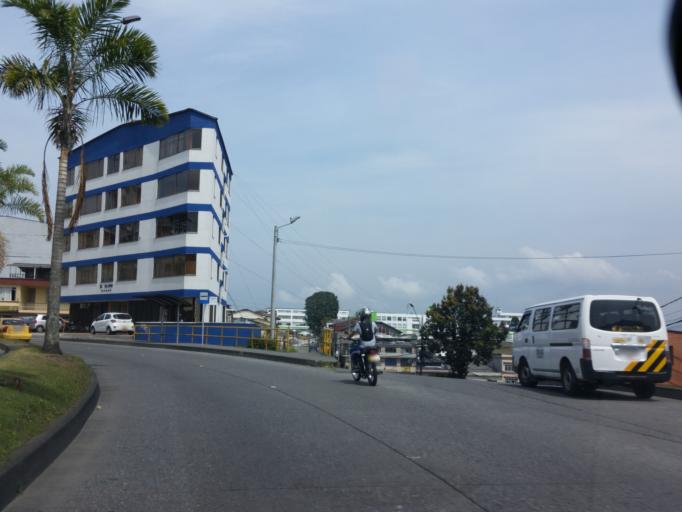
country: CO
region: Caldas
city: Manizales
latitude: 5.0728
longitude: -75.5198
